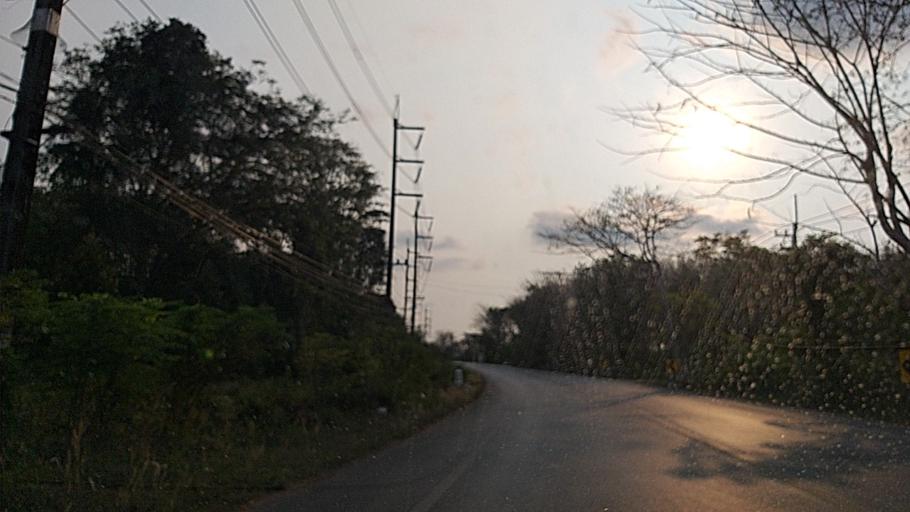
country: TH
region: Trat
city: Khao Saming
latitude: 12.2979
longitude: 102.3369
